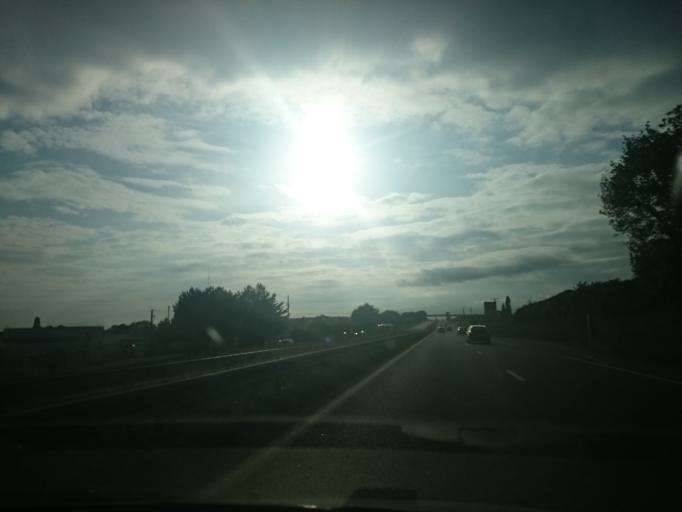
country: FR
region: Brittany
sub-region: Departement du Morbihan
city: Theix
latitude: 47.6341
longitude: -2.6595
